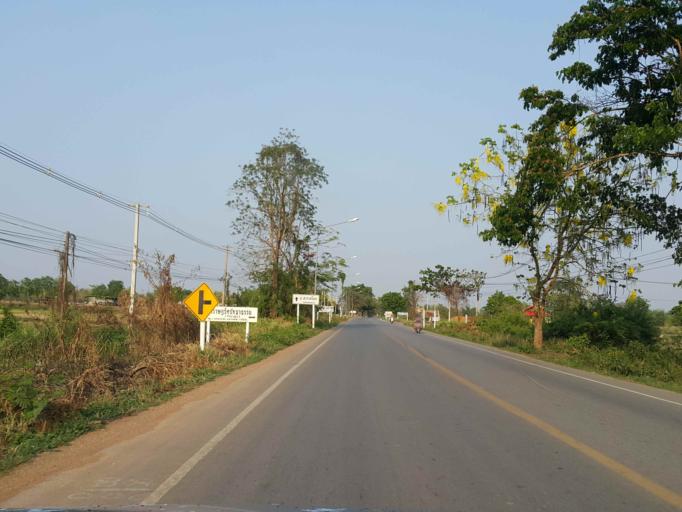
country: TH
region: Sukhothai
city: Sawankhalok
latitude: 17.3095
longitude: 99.7928
